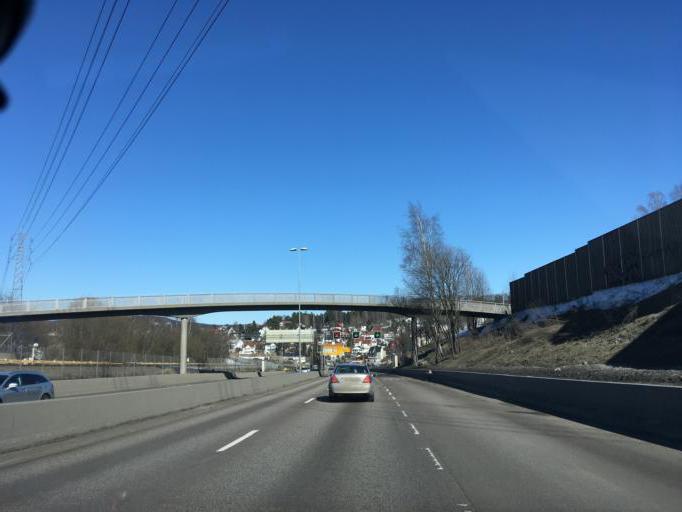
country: NO
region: Oslo
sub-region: Oslo
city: Oslo
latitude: 59.9013
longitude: 10.8183
